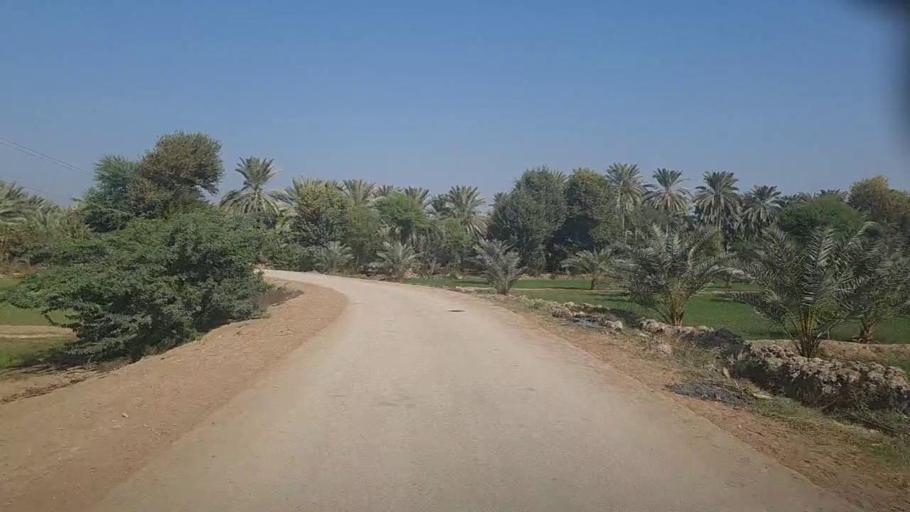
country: PK
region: Sindh
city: Kot Diji
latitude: 27.4213
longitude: 68.7064
